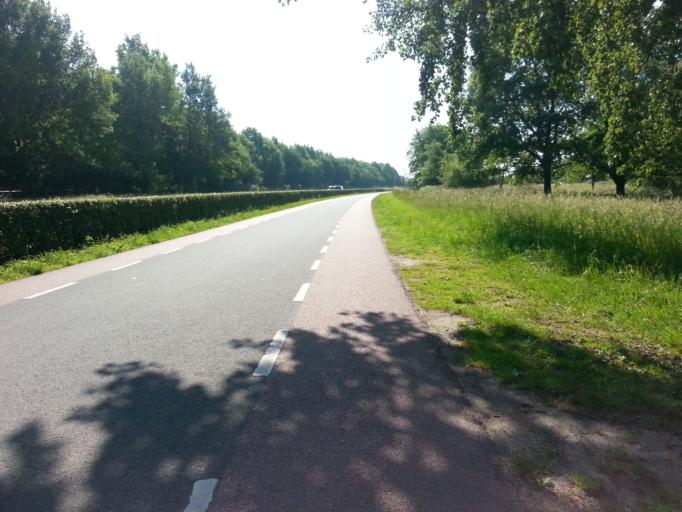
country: NL
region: Utrecht
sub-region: Gemeente Utrechtse Heuvelrug
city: Driebergen-Rijsenburg
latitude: 52.0082
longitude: 5.2857
